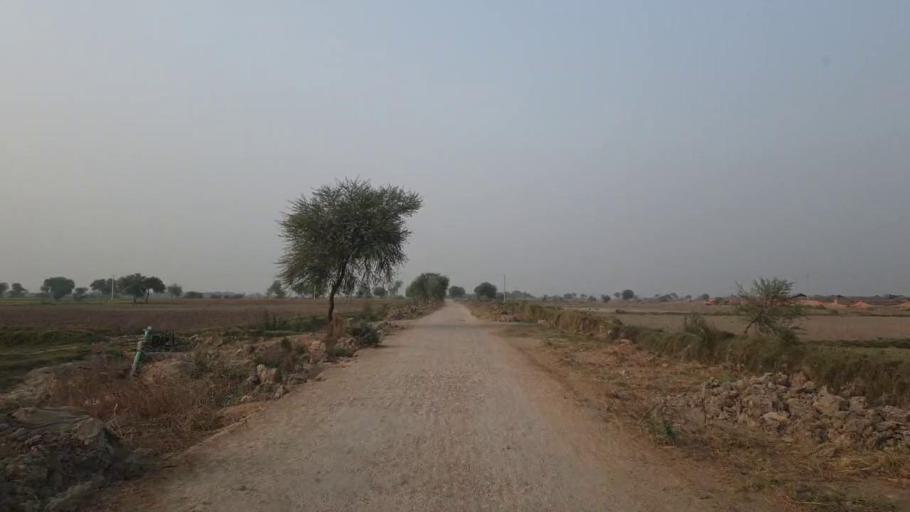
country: PK
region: Sindh
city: Mirpur Batoro
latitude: 24.6573
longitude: 68.3785
